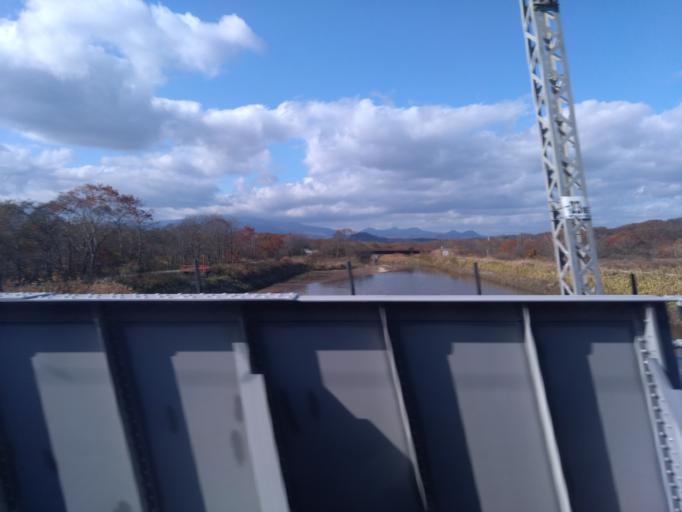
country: JP
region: Hokkaido
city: Shiraoi
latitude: 42.5316
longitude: 141.3226
